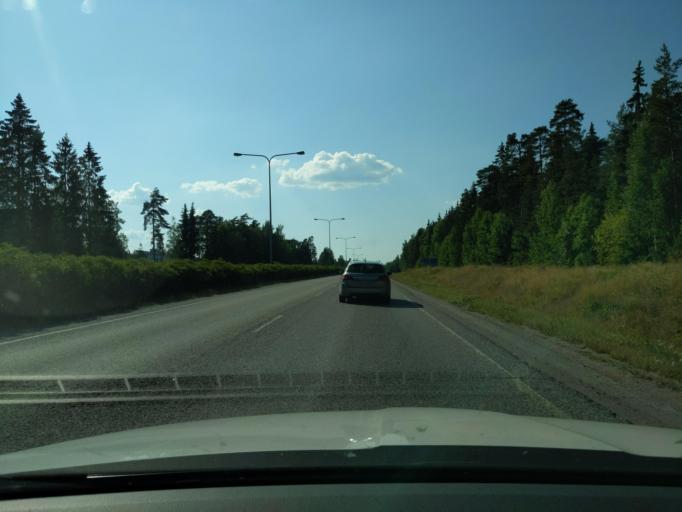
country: FI
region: Paijanne Tavastia
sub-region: Lahti
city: Lahti
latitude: 60.9801
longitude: 25.6030
